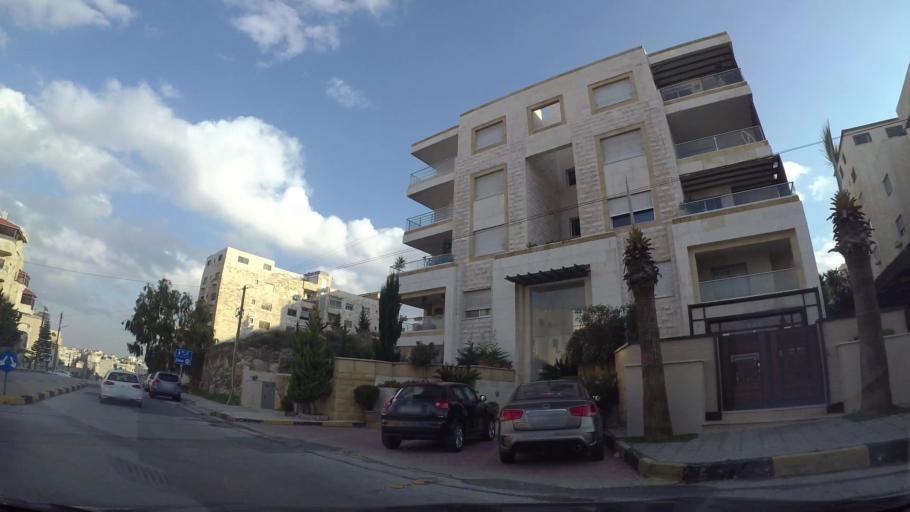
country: JO
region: Amman
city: Al Jubayhah
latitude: 31.9767
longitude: 35.8811
